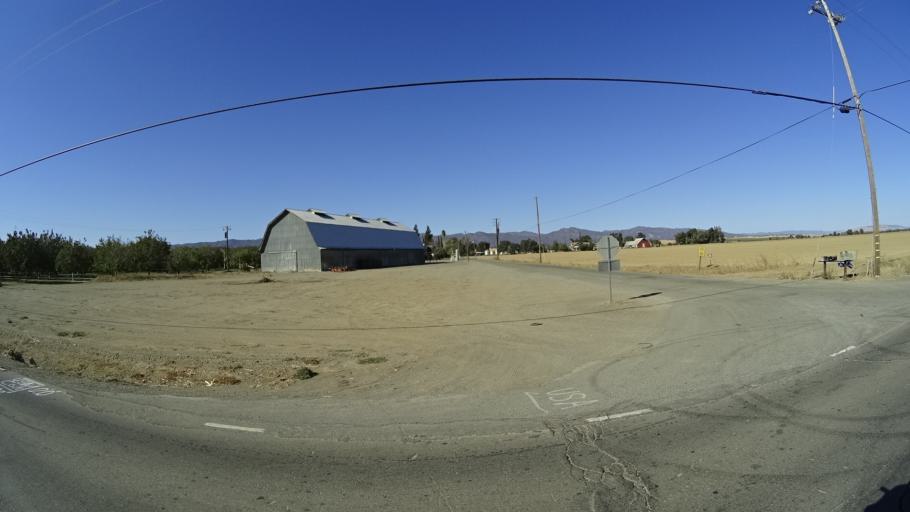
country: US
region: California
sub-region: Yolo County
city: Winters
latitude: 38.5838
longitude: -121.9712
